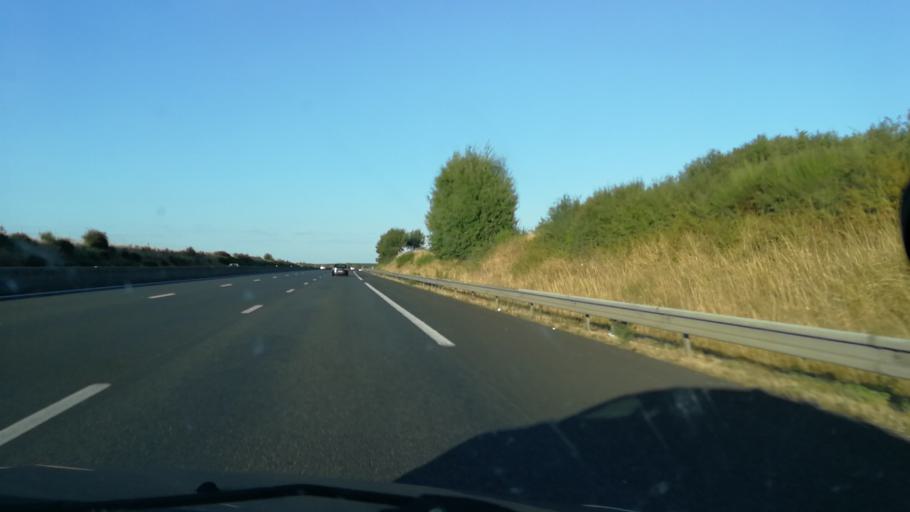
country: FR
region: Centre
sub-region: Departement d'Indre-et-Loire
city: Reugny
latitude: 47.5045
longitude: 0.8696
